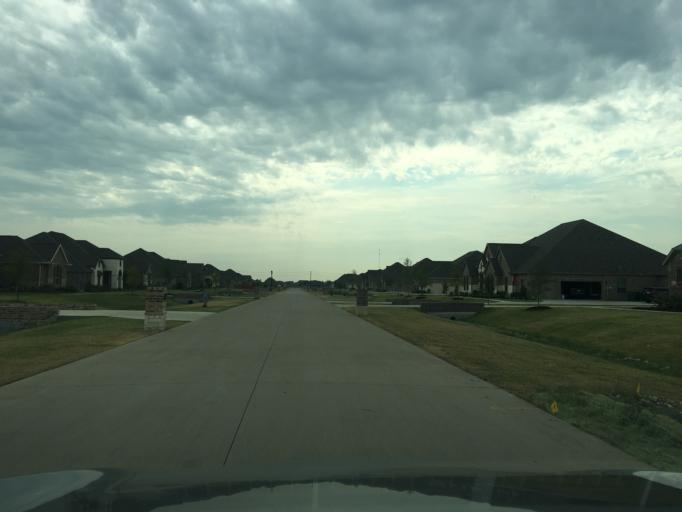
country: US
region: Texas
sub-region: Collin County
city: Parker
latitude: 33.0674
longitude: -96.6061
